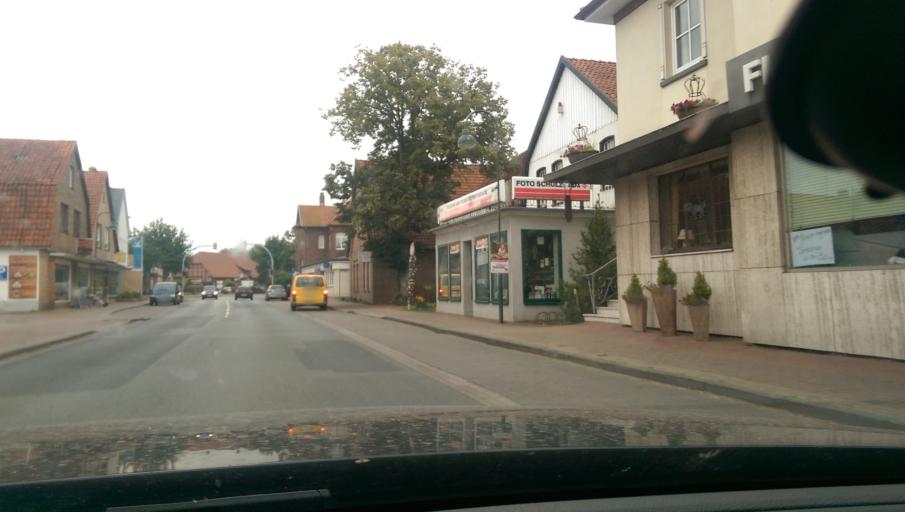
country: DE
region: Lower Saxony
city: Rehburg-Loccum
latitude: 52.4758
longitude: 9.2294
